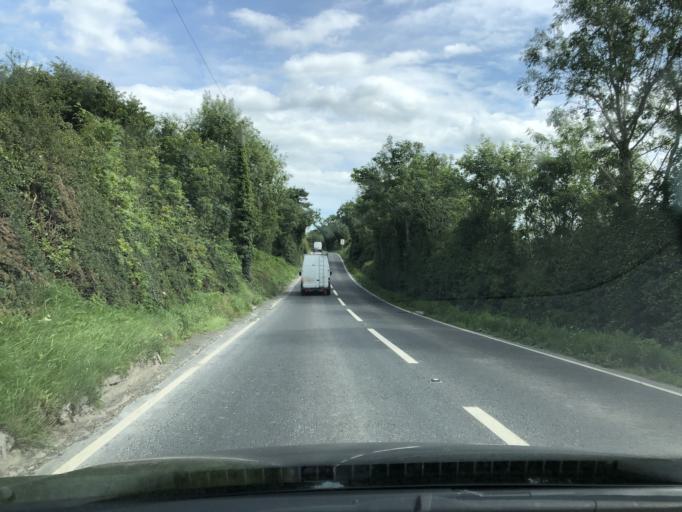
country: GB
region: Northern Ireland
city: Ballynahinch
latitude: 54.4175
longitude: -5.9100
